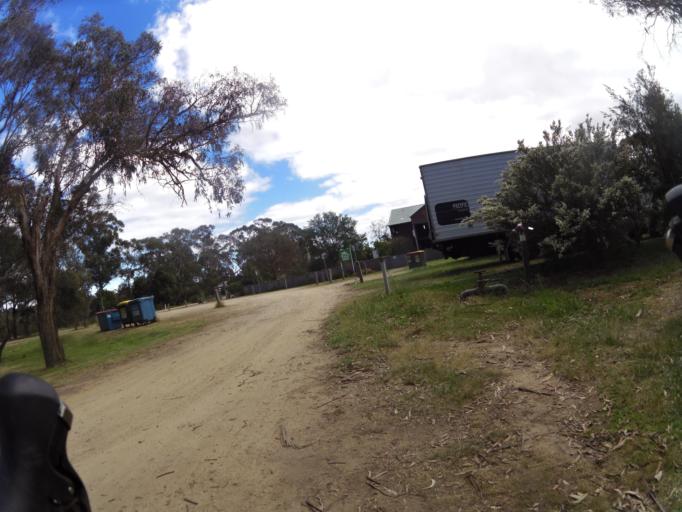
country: AU
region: Victoria
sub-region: Mornington Peninsula
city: Mount Martha
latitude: -38.2733
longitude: 145.0410
